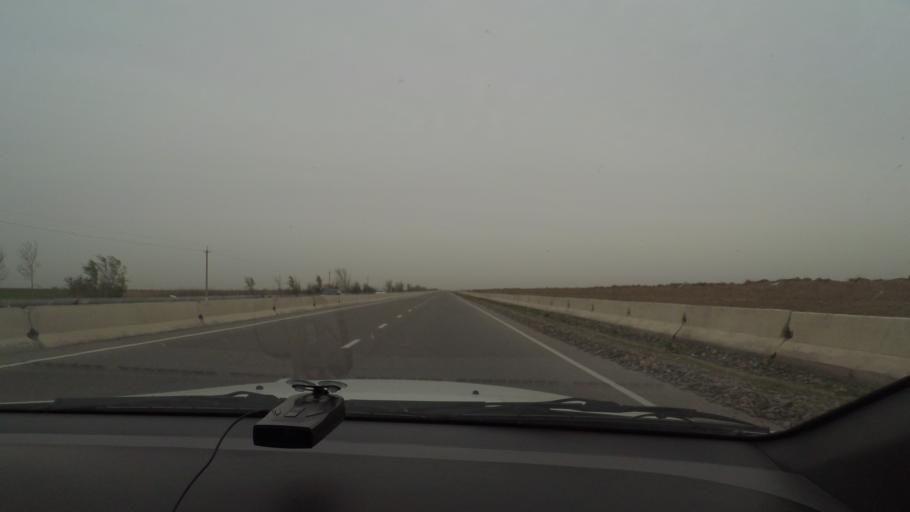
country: UZ
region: Jizzax
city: Dustlik
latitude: 40.4334
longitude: 68.2288
